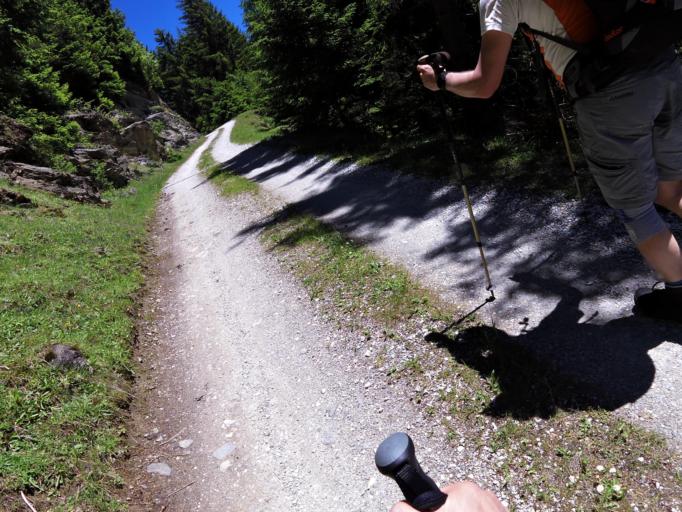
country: AT
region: Tyrol
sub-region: Politischer Bezirk Innsbruck Land
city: Neustift im Stubaital
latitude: 47.1135
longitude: 11.2916
